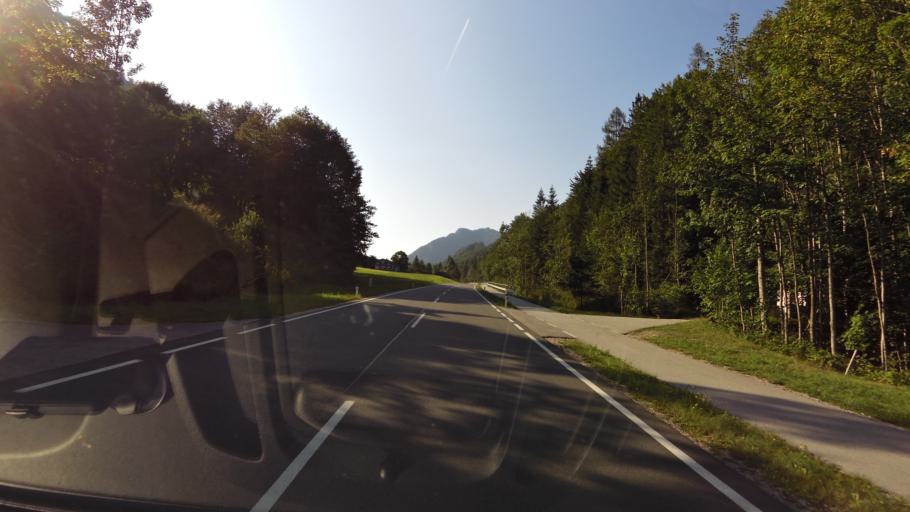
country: AT
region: Salzburg
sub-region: Politischer Bezirk Salzburg-Umgebung
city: Sankt Gilgen
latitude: 47.7864
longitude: 13.3400
